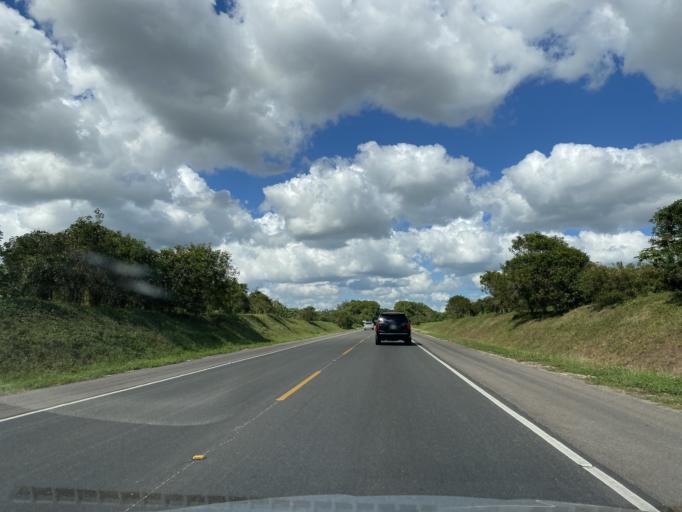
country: DO
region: Monte Plata
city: Monte Plata
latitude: 18.7444
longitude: -69.7648
